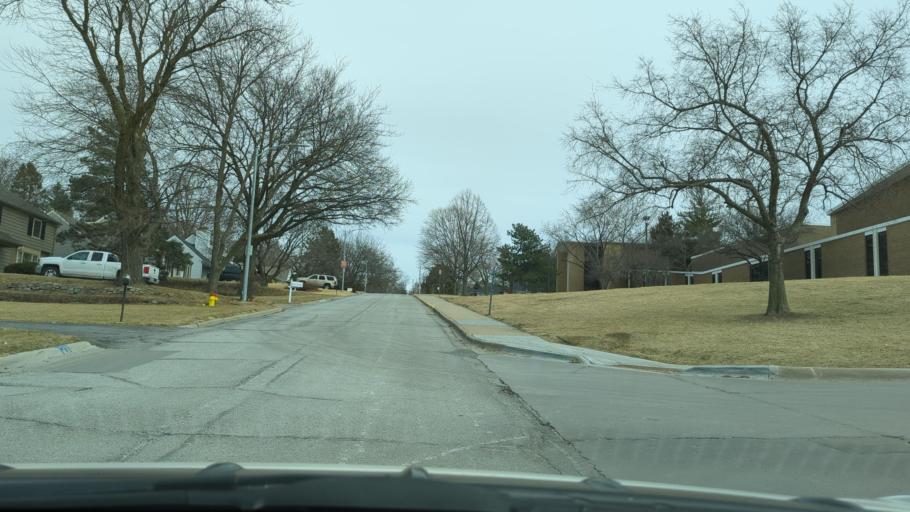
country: US
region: Nebraska
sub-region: Douglas County
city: Ralston
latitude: 41.2669
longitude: -96.0214
